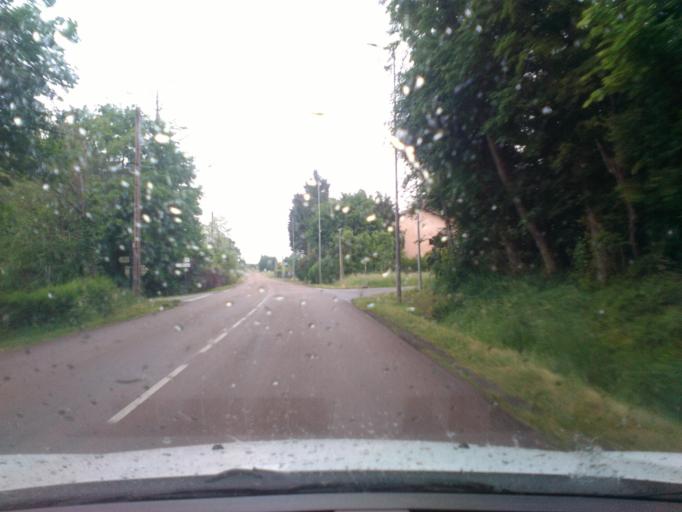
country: FR
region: Lorraine
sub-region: Departement des Vosges
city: Rambervillers
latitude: 48.3566
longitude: 6.6298
